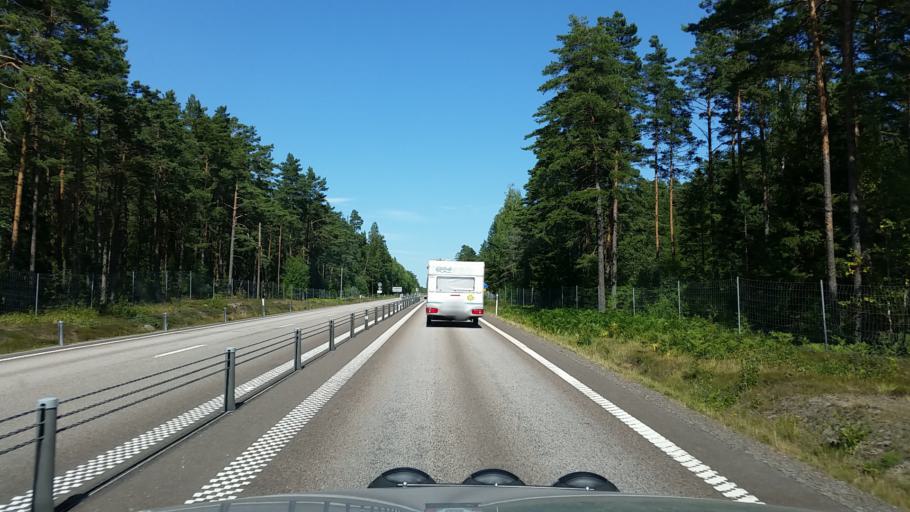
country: SE
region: Vaestra Goetaland
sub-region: Melleruds Kommun
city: Mellerud
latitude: 58.8285
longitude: 12.5297
